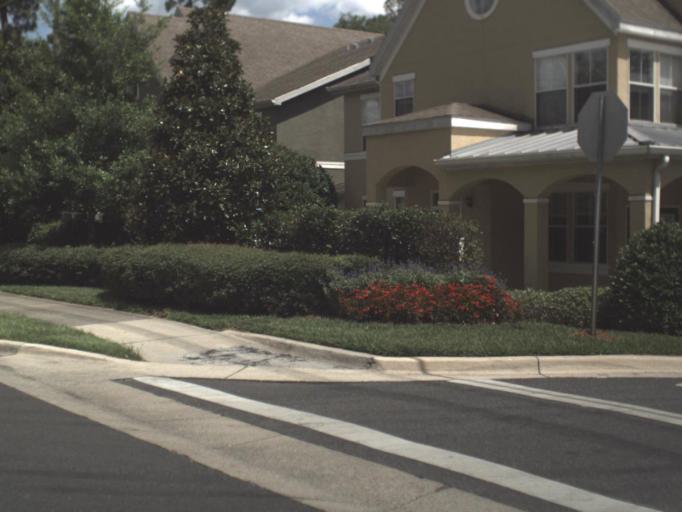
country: US
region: Florida
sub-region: Alachua County
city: Gainesville
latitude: 29.6884
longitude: -82.3563
